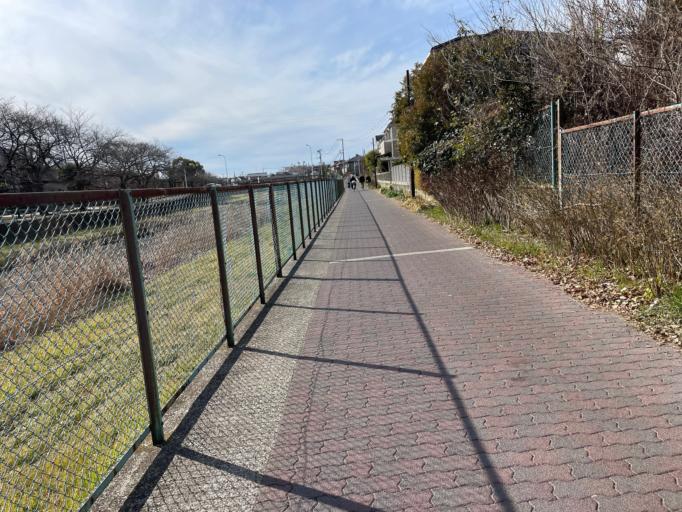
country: JP
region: Tokyo
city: Higashimurayama-shi
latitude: 35.7651
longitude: 139.4853
